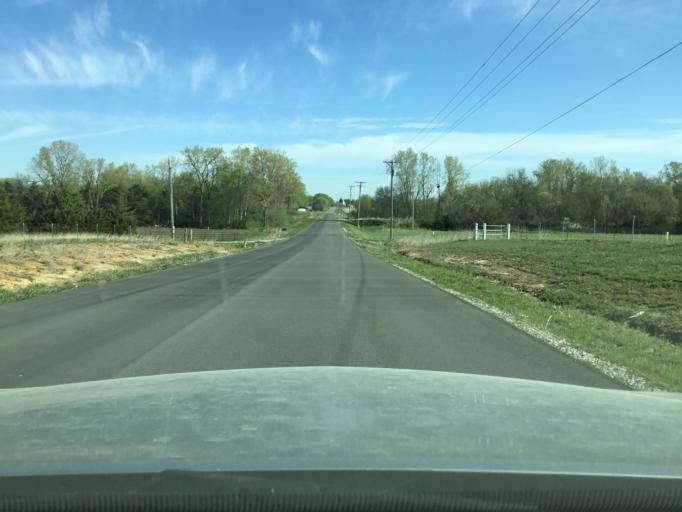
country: US
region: Kansas
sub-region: Neosho County
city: Chanute
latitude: 37.6557
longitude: -95.4435
